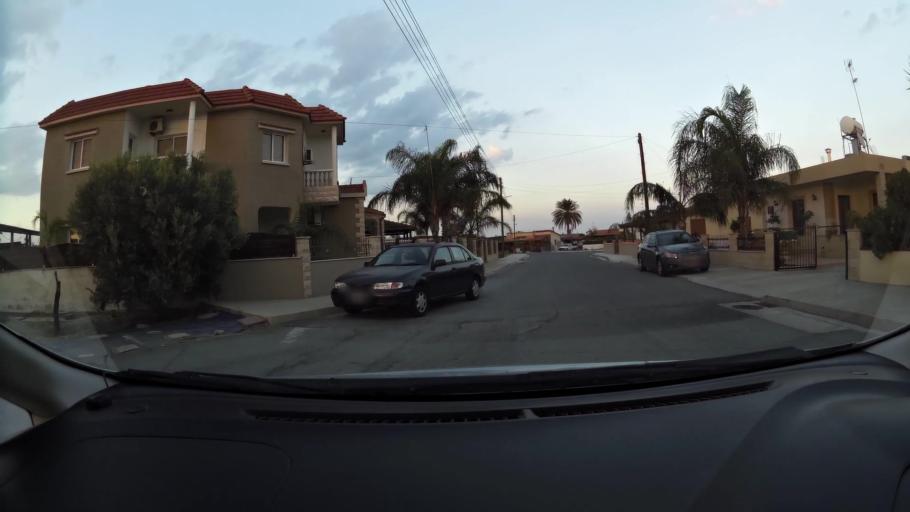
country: CY
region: Larnaka
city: Dhromolaxia
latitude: 34.8753
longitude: 33.5823
